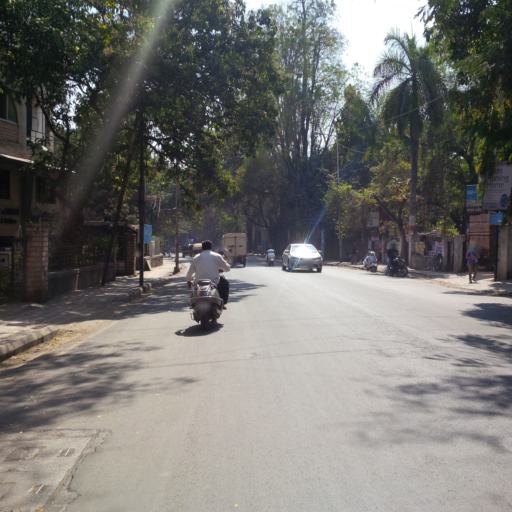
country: IN
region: Maharashtra
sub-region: Pune Division
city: Pune
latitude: 18.5141
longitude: 73.8288
